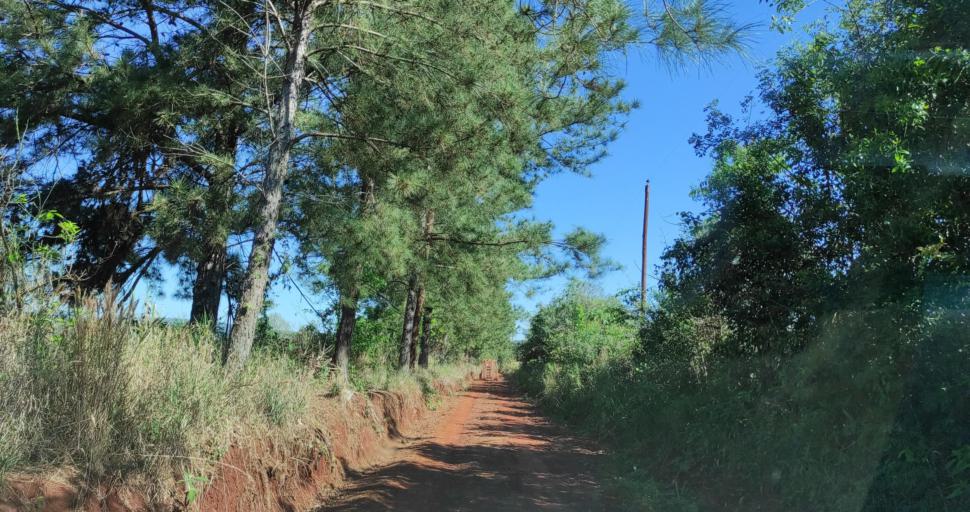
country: AR
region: Misiones
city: Capiovi
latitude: -26.9133
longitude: -55.0199
